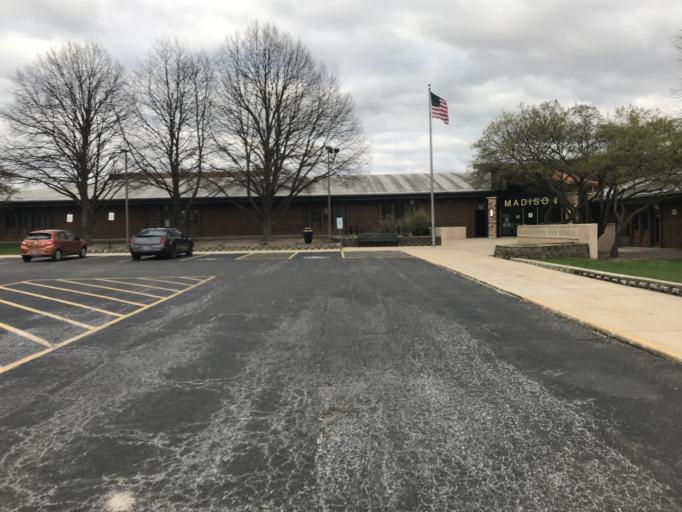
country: US
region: Illinois
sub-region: Will County
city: Bolingbrook
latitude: 41.7353
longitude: -88.1105
